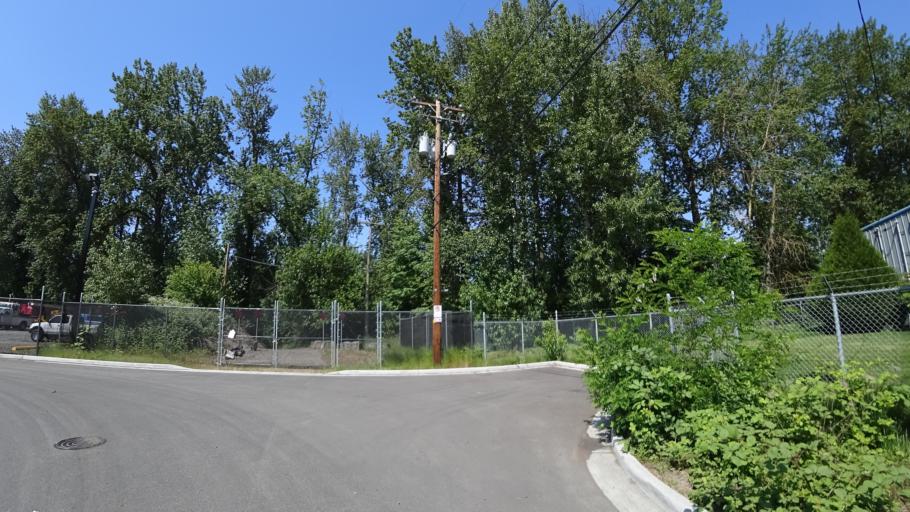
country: US
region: Oregon
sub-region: Multnomah County
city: Lents
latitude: 45.5627
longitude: -122.5474
